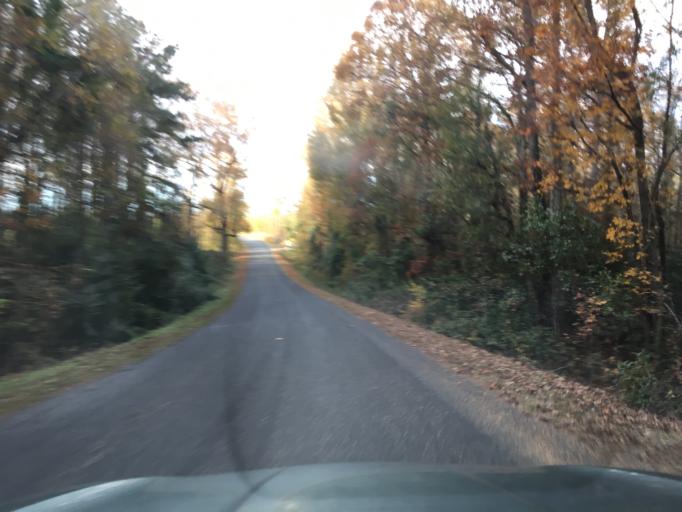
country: US
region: South Carolina
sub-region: Barnwell County
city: Williston
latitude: 33.6728
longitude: -81.3706
